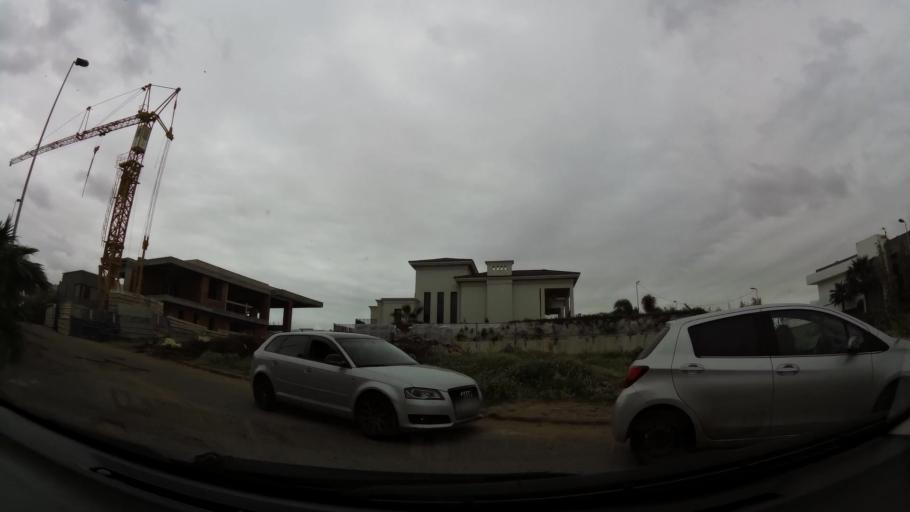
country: MA
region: Grand Casablanca
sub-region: Casablanca
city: Casablanca
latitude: 33.6009
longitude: -7.6595
